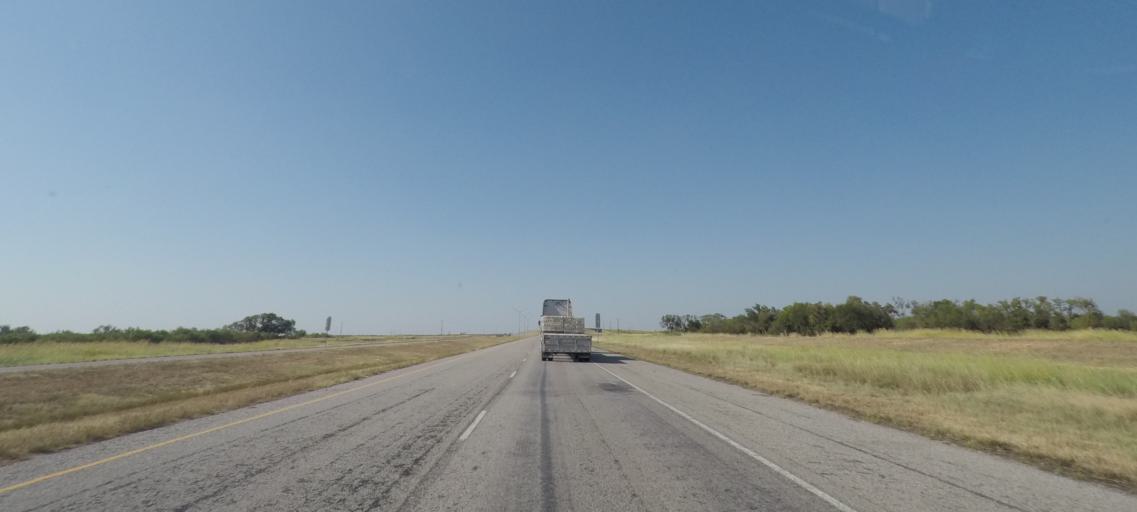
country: US
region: Texas
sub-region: Baylor County
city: Seymour
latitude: 33.6060
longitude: -99.2423
